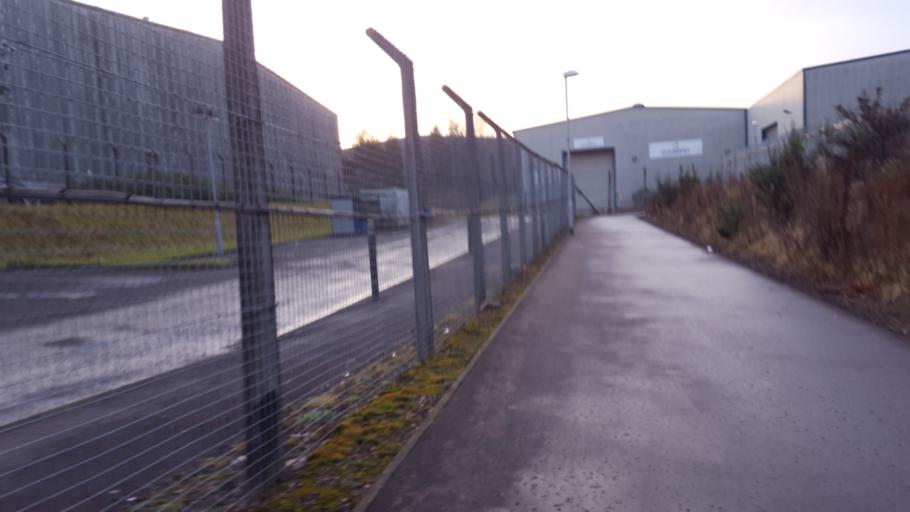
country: GB
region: Scotland
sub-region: West Lothian
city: Livingston
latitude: 55.9157
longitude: -3.5152
